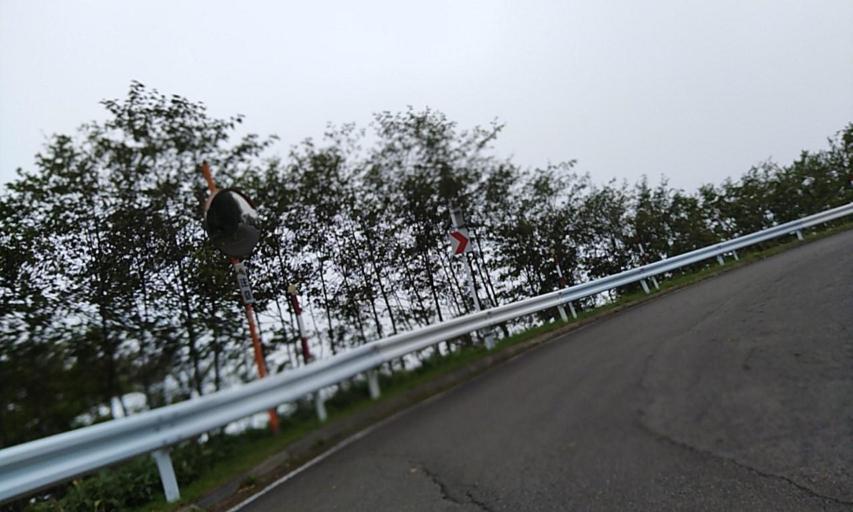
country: JP
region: Hokkaido
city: Bihoro
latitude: 43.5754
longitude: 144.2392
